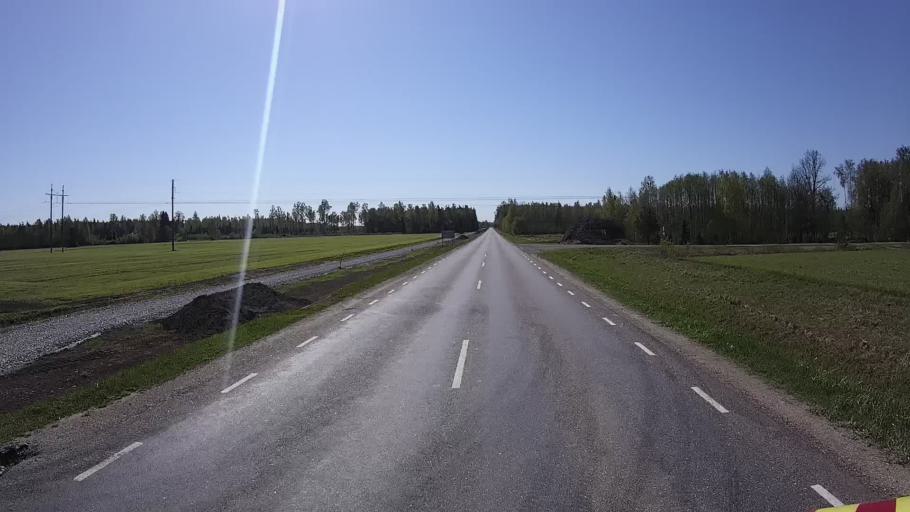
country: EE
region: Paernumaa
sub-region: Tootsi vald
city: Tootsi
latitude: 58.5023
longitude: 24.7982
